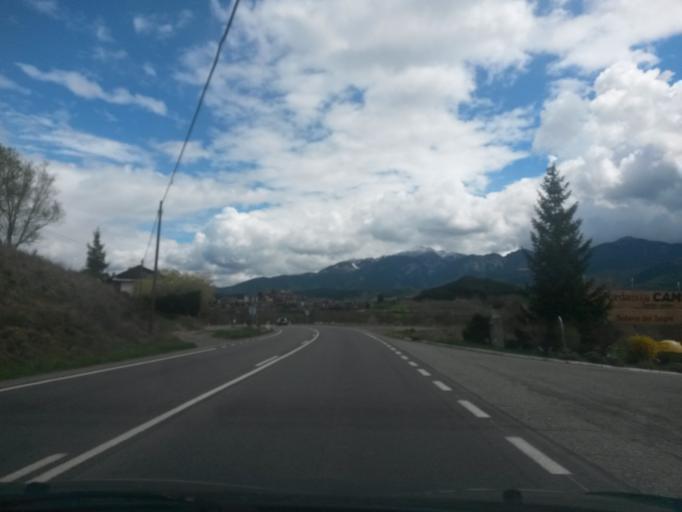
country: ES
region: Catalonia
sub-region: Provincia de Lleida
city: Bellver de Cerdanya
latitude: 42.3730
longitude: 1.7604
